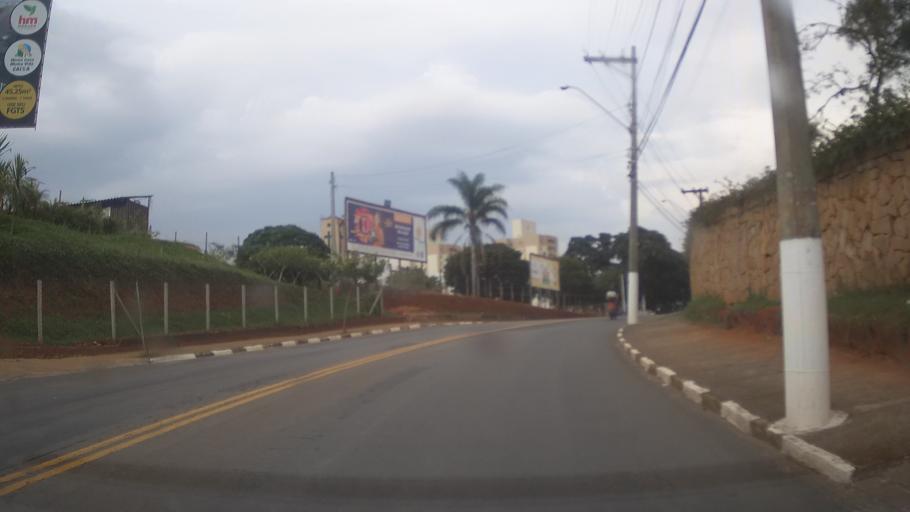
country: BR
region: Sao Paulo
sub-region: Itupeva
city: Itupeva
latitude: -23.1652
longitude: -47.0554
